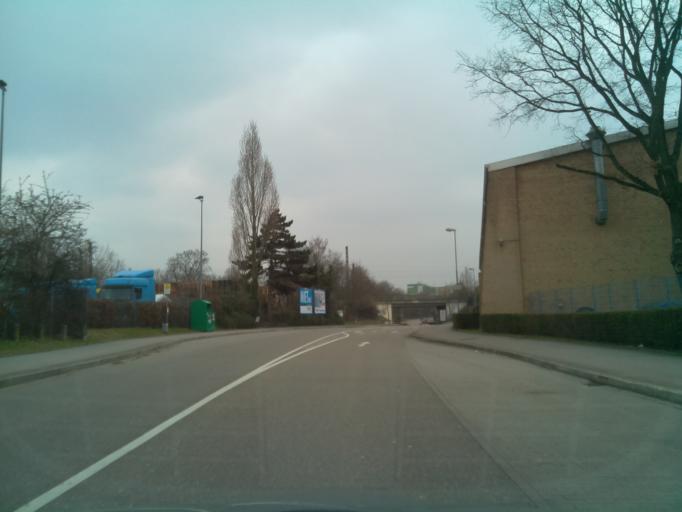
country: DE
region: Baden-Wuerttemberg
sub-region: Karlsruhe Region
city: Ladenburg
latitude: 49.4792
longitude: 8.6046
